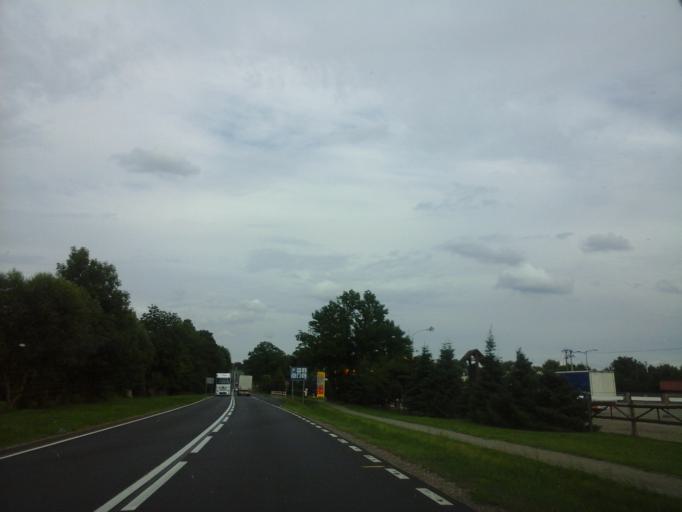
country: PL
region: West Pomeranian Voivodeship
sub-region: Powiat stargardzki
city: Suchan
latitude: 53.2768
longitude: 15.3358
